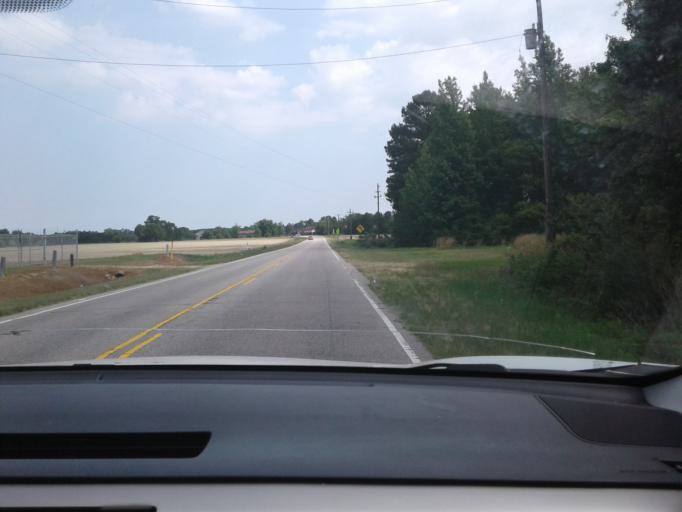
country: US
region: North Carolina
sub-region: Harnett County
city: Coats
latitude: 35.3678
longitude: -78.6625
